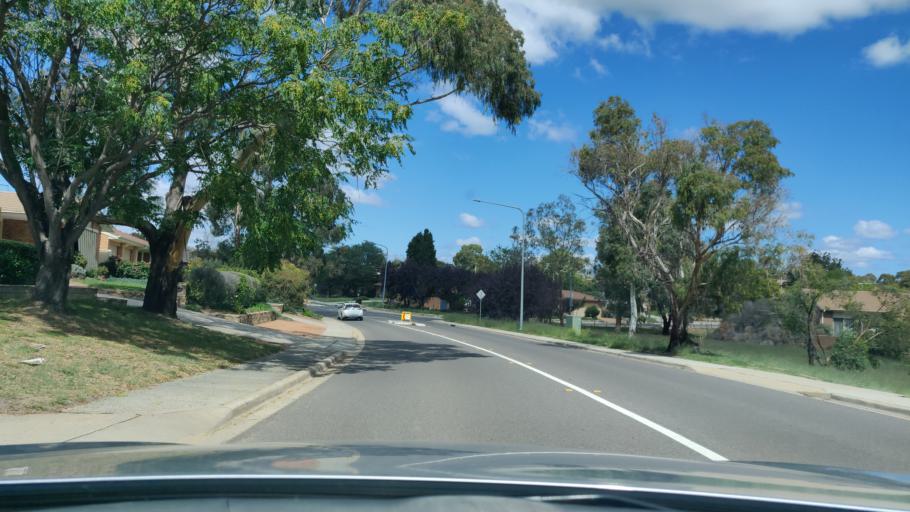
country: AU
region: Australian Capital Territory
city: Macarthur
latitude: -35.4297
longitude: 149.0745
